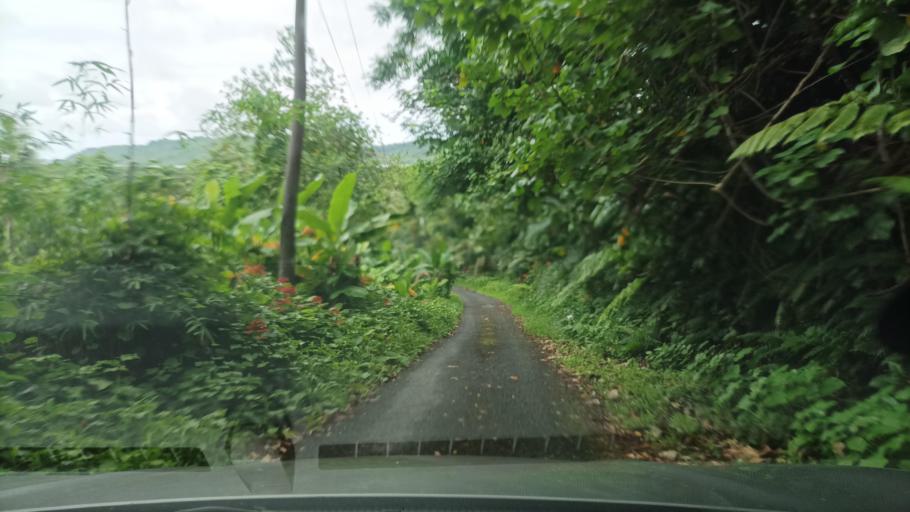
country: FM
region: Pohnpei
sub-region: Kolonia Municipality
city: Kolonia
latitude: 6.9412
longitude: 158.2733
